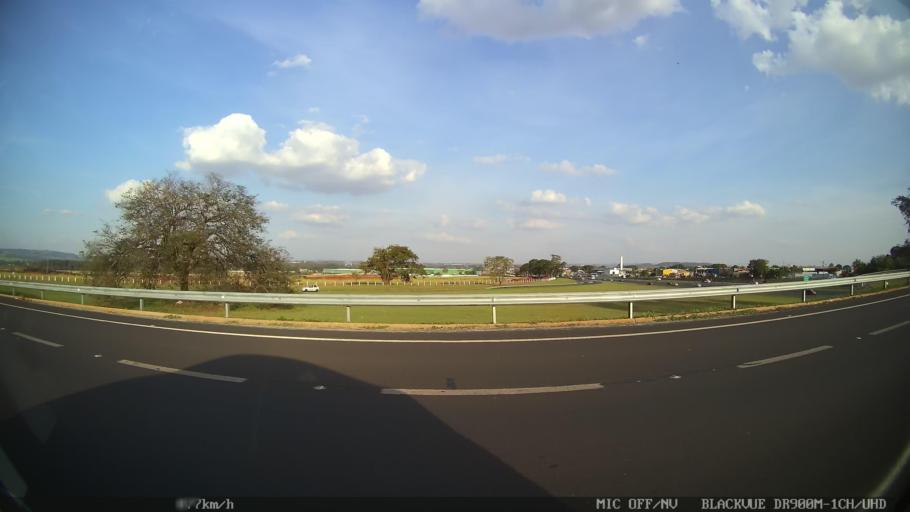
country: BR
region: Sao Paulo
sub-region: Ribeirao Preto
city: Ribeirao Preto
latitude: -21.1133
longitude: -47.7789
